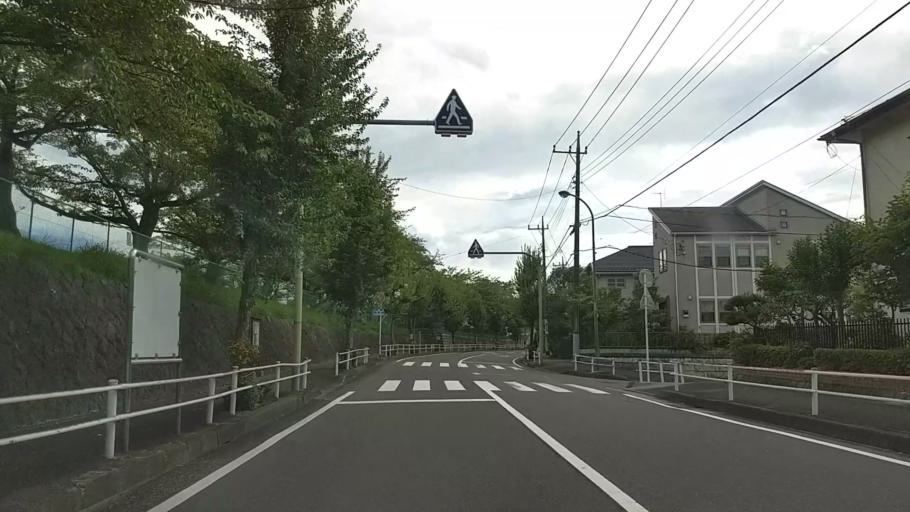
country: JP
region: Tokyo
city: Hachioji
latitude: 35.6304
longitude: 139.3579
